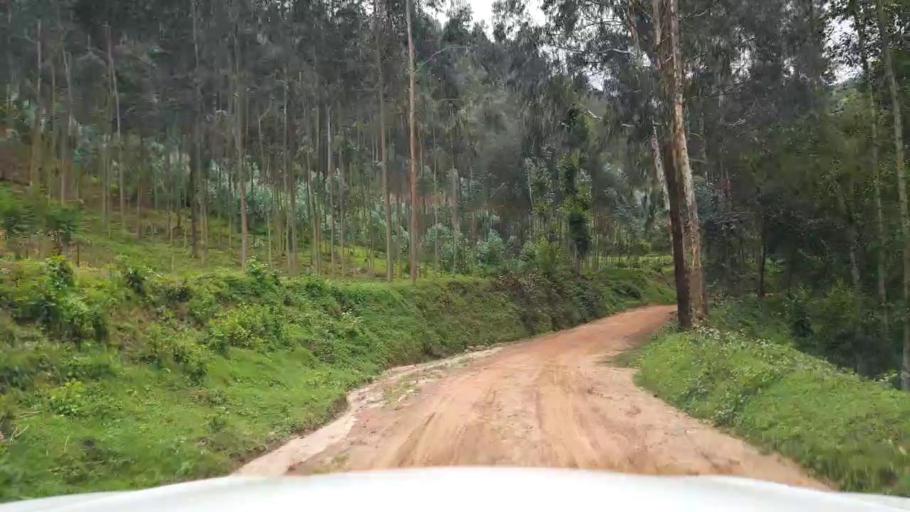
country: UG
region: Western Region
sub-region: Kabale District
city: Kabale
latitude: -1.4237
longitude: 29.8675
